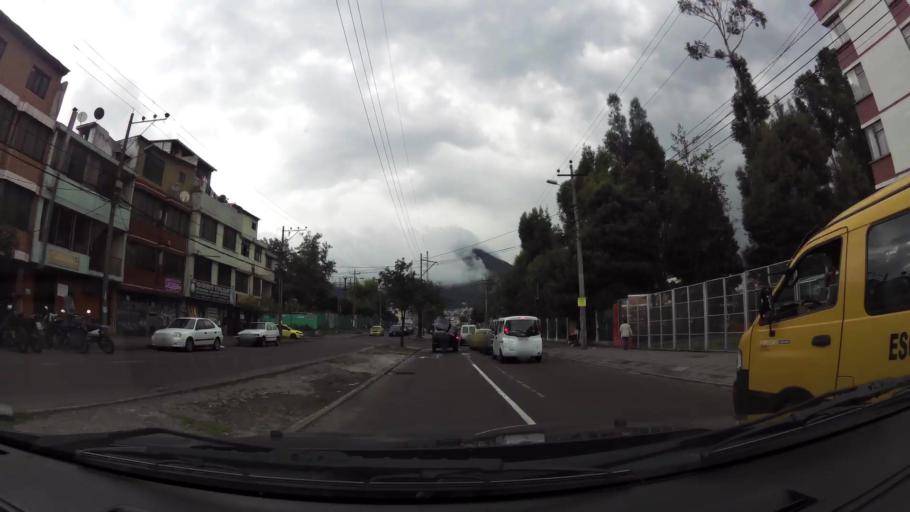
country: EC
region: Pichincha
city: Quito
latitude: -0.2662
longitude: -78.5351
